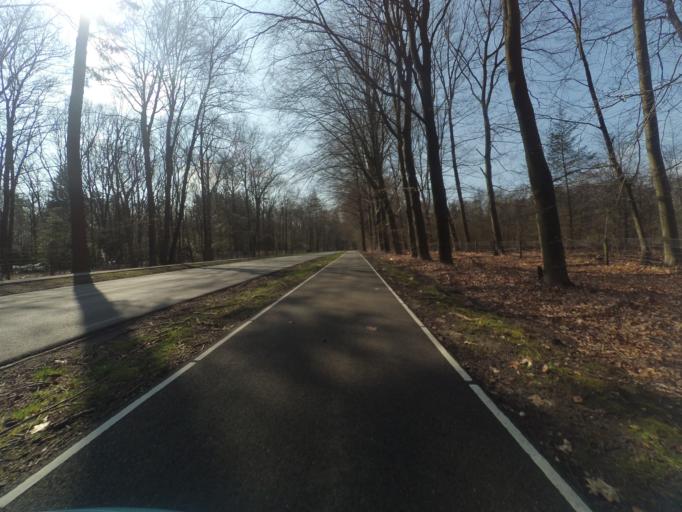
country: NL
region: Gelderland
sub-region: Gemeente Apeldoorn
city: Beekbergen
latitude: 52.1395
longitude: 5.8861
